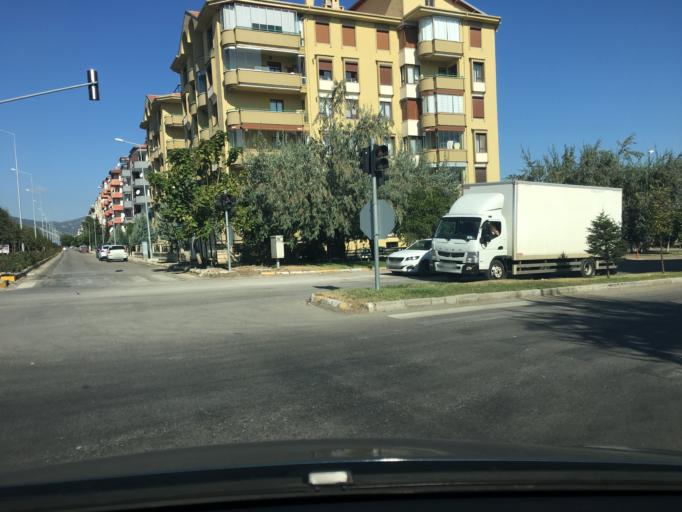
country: TR
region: Isparta
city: Isparta
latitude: 37.7884
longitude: 30.5549
